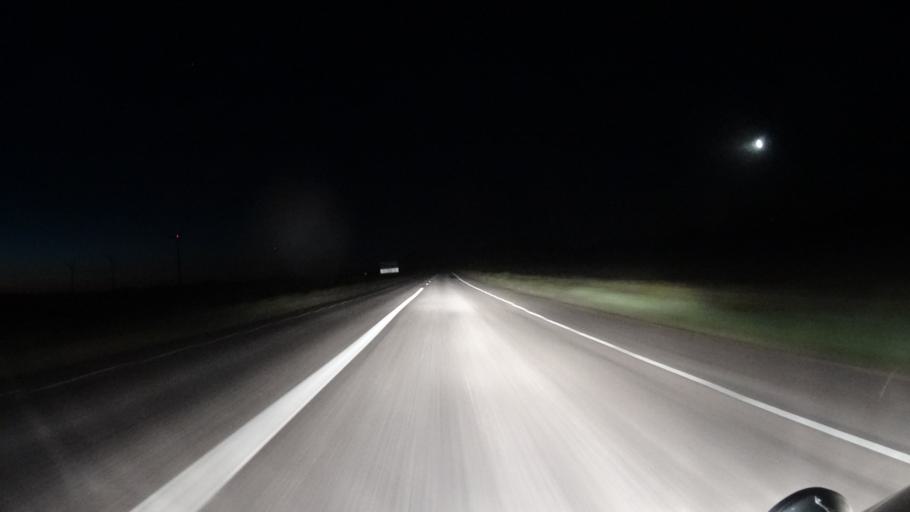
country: SE
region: OEstergoetland
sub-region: Vadstena Kommun
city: Herrestad
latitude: 58.2945
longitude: 14.7914
